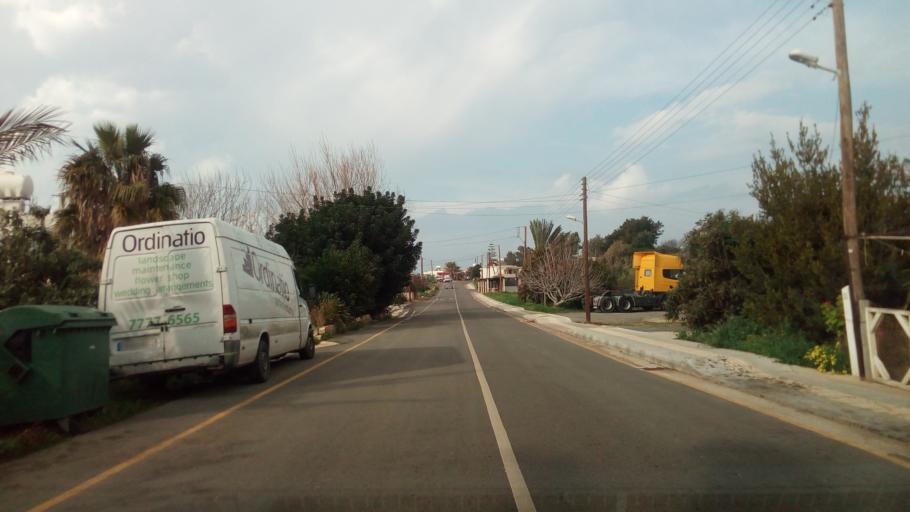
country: CY
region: Lefkosia
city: Kato Pyrgos
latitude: 35.1633
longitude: 32.5468
